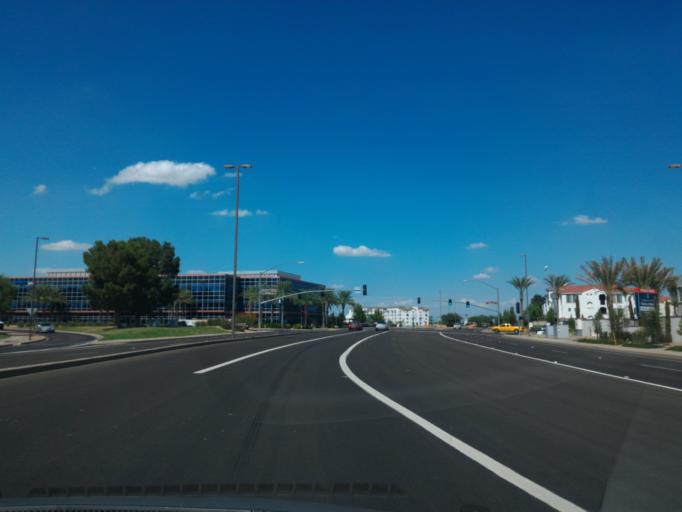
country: US
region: Arizona
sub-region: Maricopa County
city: Sun Lakes
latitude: 33.2552
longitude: -111.8843
